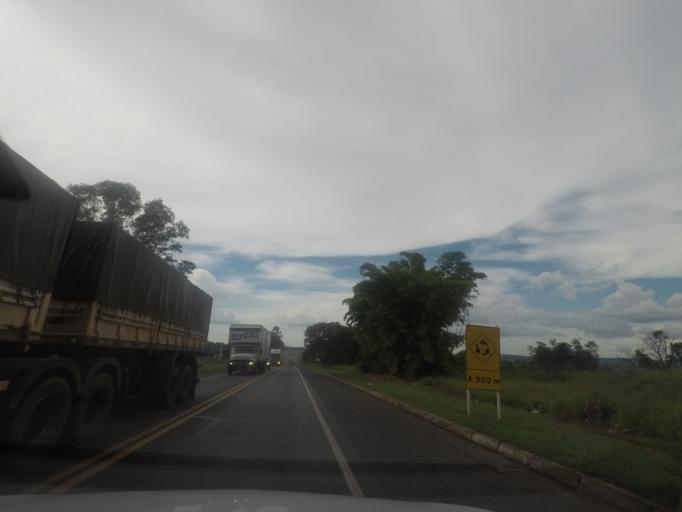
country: BR
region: Minas Gerais
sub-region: Prata
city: Prata
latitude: -19.3079
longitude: -48.9071
